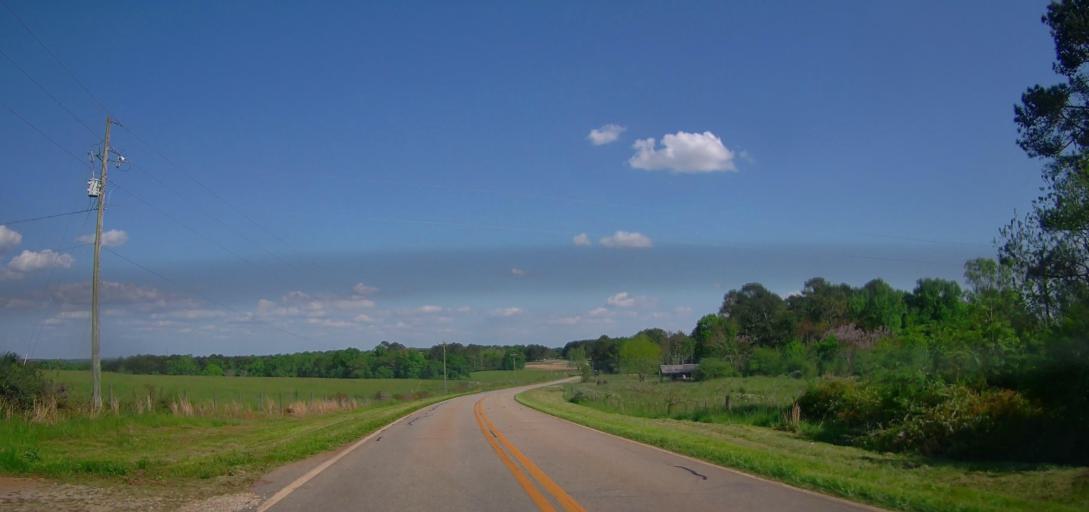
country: US
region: Georgia
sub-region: Morgan County
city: Madison
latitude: 33.6623
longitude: -83.4806
